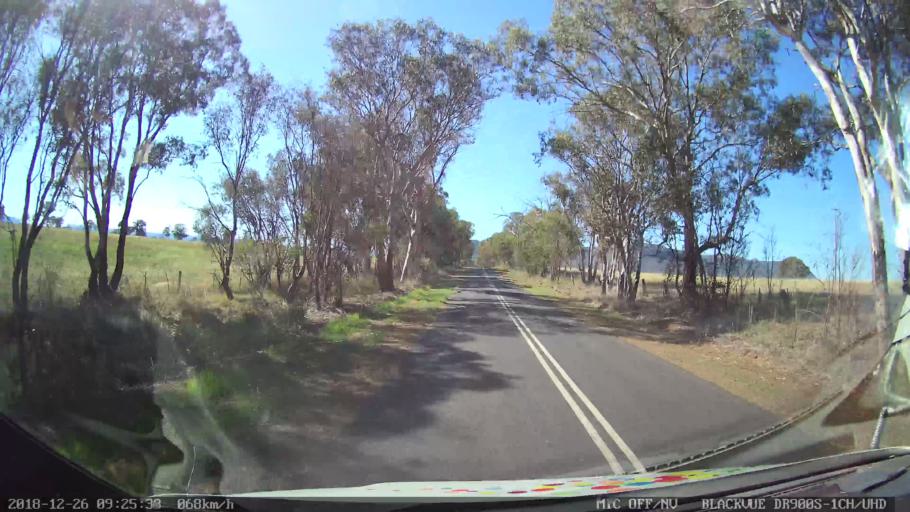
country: AU
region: New South Wales
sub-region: Mid-Western Regional
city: Kandos
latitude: -32.8217
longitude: 150.0045
